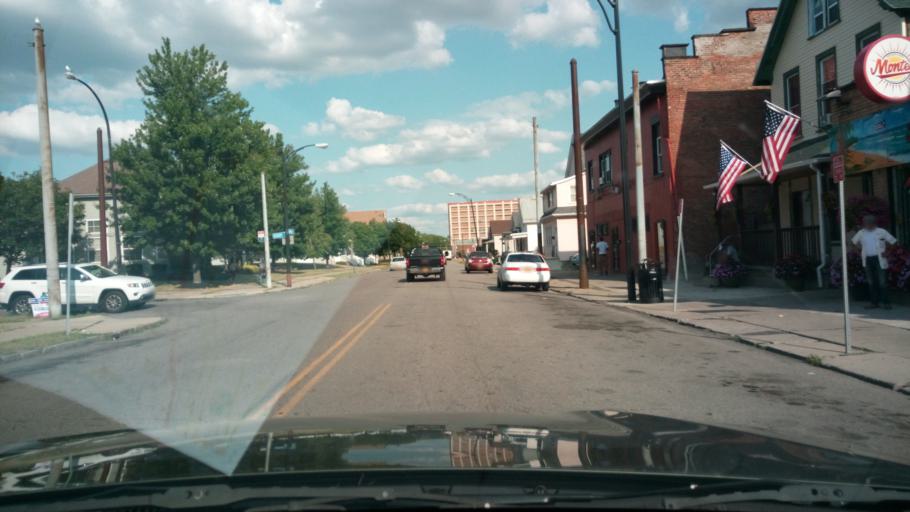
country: US
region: New York
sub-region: Erie County
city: Buffalo
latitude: 42.8792
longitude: -78.8606
